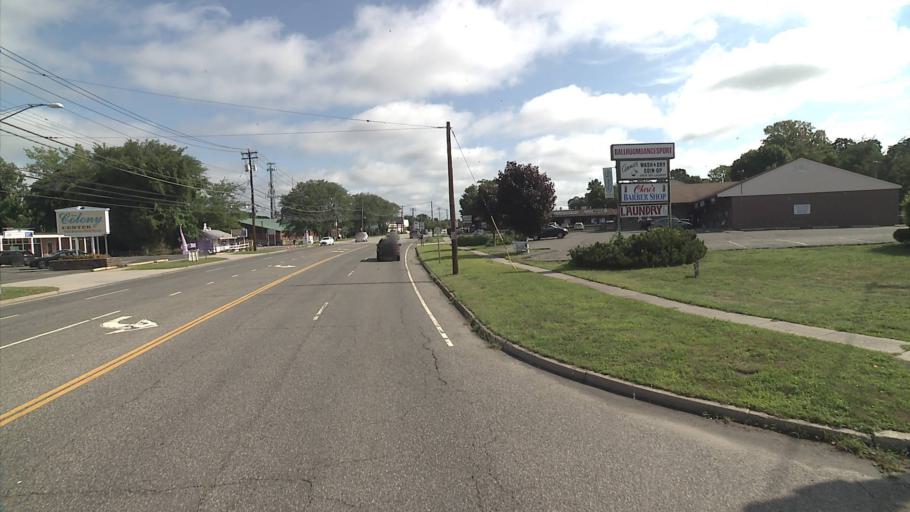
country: US
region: Connecticut
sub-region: New Haven County
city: City of Milford (balance)
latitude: 41.2262
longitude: -73.0708
